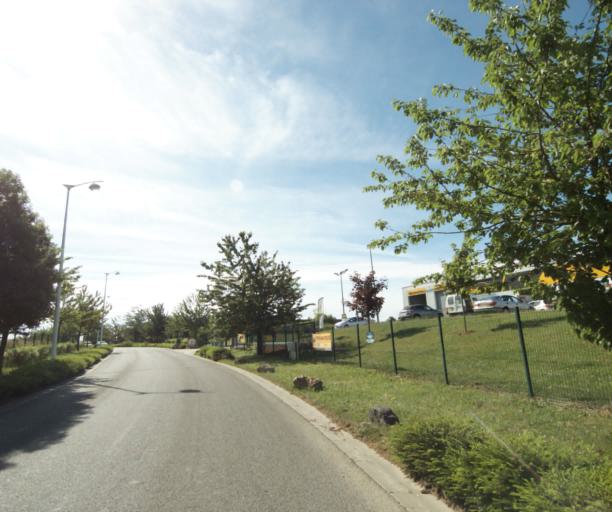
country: FR
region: Centre
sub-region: Departement d'Eure-et-Loir
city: Luce
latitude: 48.4238
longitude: 1.4384
